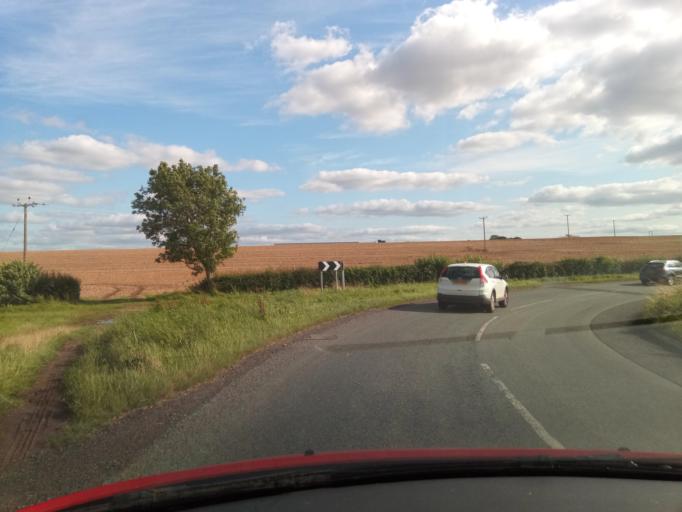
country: GB
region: Scotland
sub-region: The Scottish Borders
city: Coldstream
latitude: 55.7117
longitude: -2.2807
